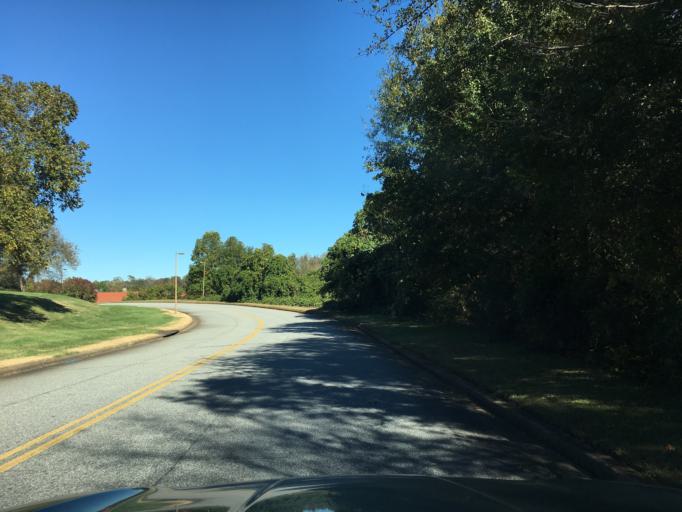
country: US
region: South Carolina
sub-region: Spartanburg County
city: Wellford
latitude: 34.9165
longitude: -82.0962
